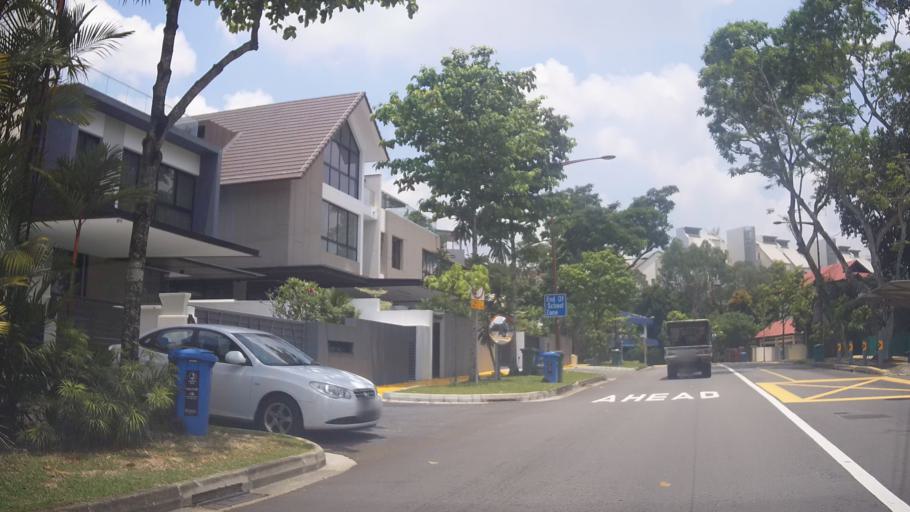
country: SG
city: Singapore
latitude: 1.3142
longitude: 103.7850
